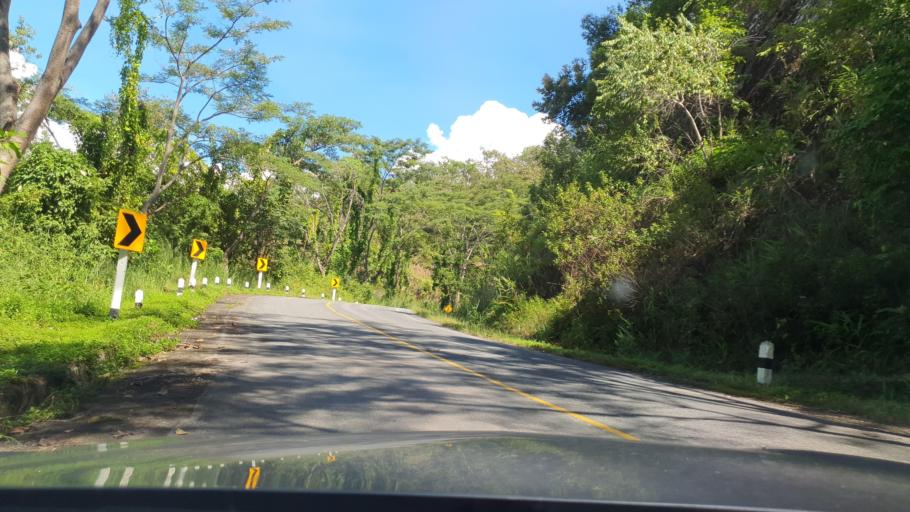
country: TH
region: Chiang Mai
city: Phrao
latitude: 19.3607
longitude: 99.2709
